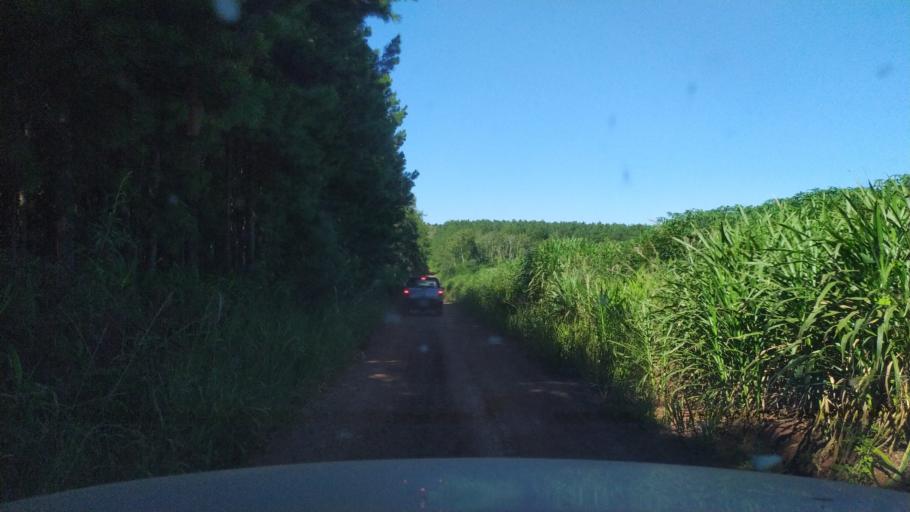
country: AR
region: Misiones
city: Caraguatay
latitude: -26.6732
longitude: -54.6977
